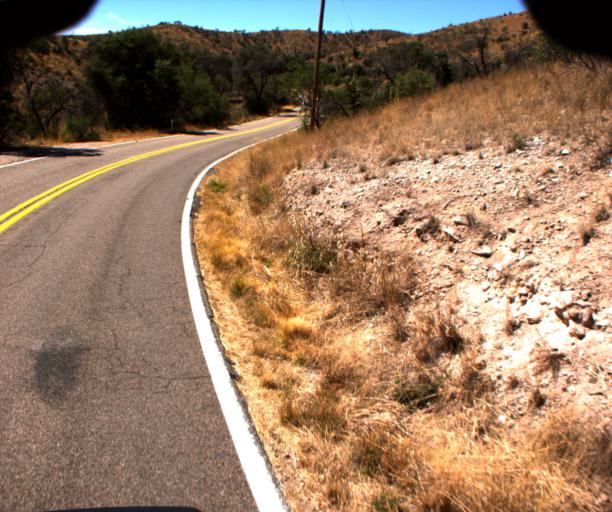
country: US
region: Arizona
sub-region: Santa Cruz County
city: Rio Rico
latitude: 31.3939
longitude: -111.0758
